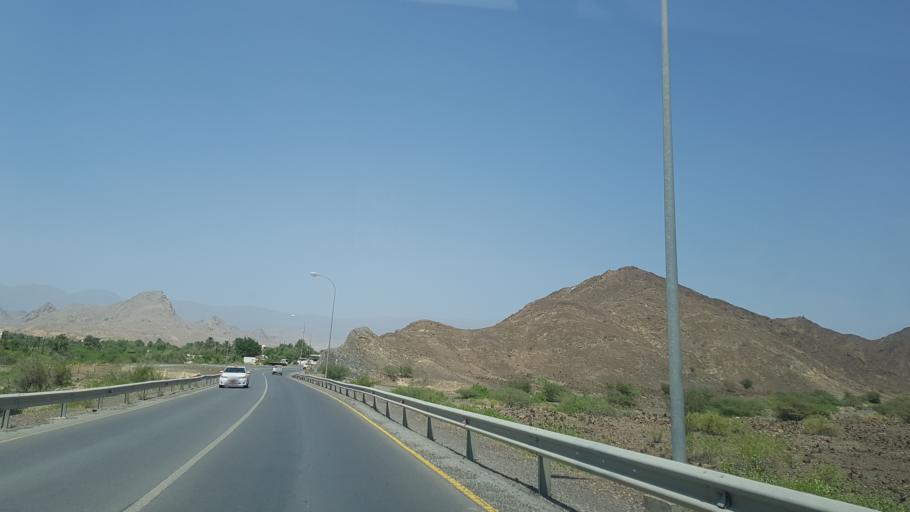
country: OM
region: Muhafazat ad Dakhiliyah
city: Bahla'
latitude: 22.9732
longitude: 57.3032
